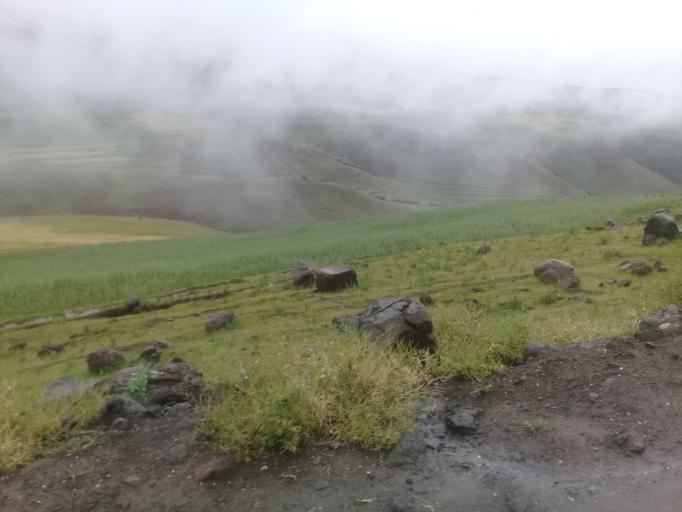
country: LS
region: Mokhotlong
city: Mokhotlong
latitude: -29.3811
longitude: 28.9816
